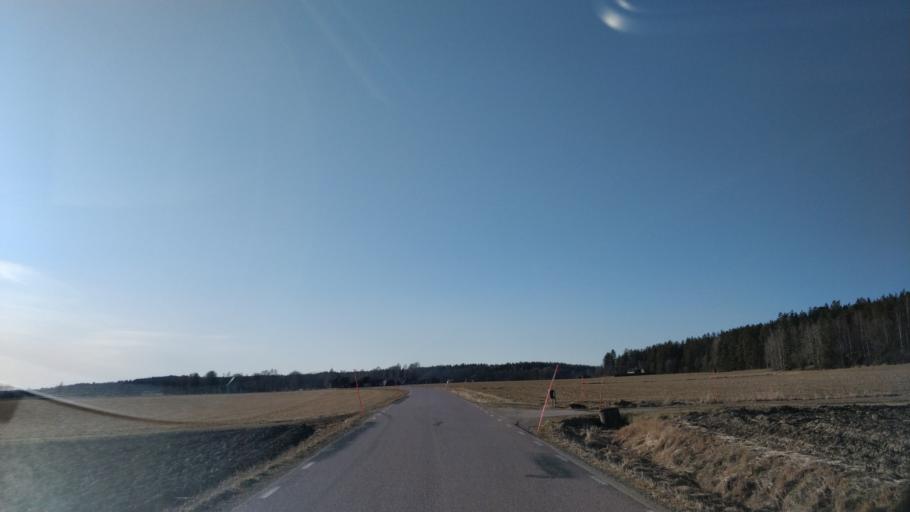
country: SE
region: Uppsala
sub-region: Enkopings Kommun
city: Orsundsbro
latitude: 59.7486
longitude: 17.1863
